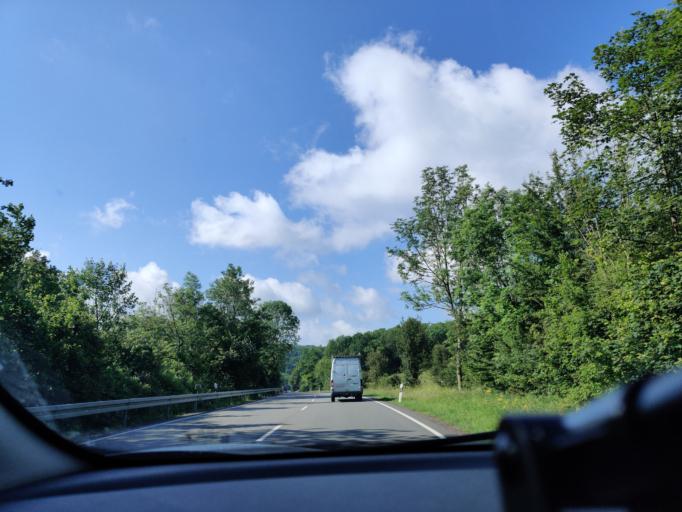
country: FR
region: Lorraine
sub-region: Departement de la Moselle
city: Bliesbruck
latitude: 49.1498
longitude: 7.1528
